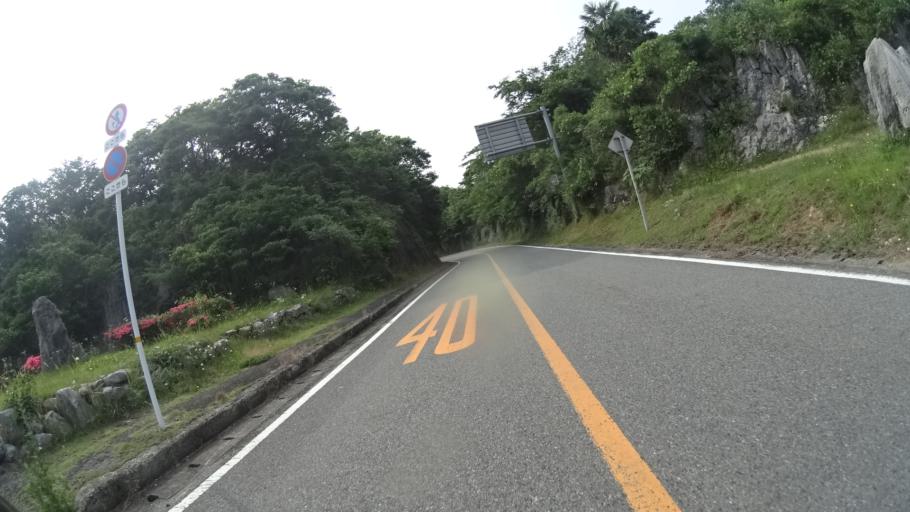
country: JP
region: Yamaguchi
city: Ogori-shimogo
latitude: 34.2346
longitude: 131.3092
